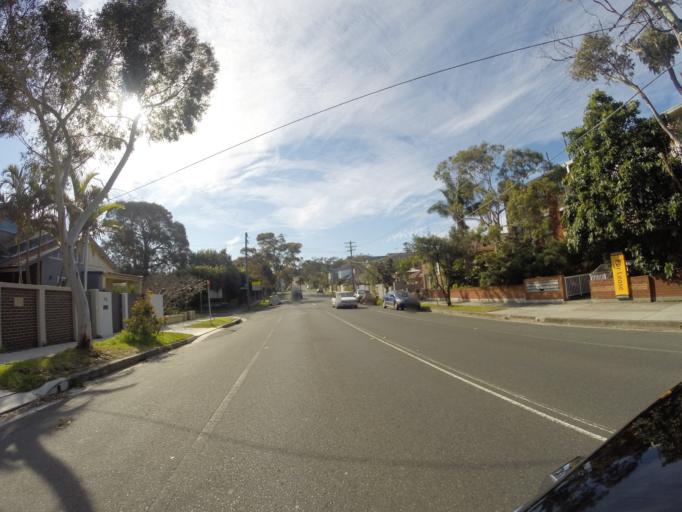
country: AU
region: New South Wales
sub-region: Randwick
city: Clovelly
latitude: -33.9099
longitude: 151.2591
